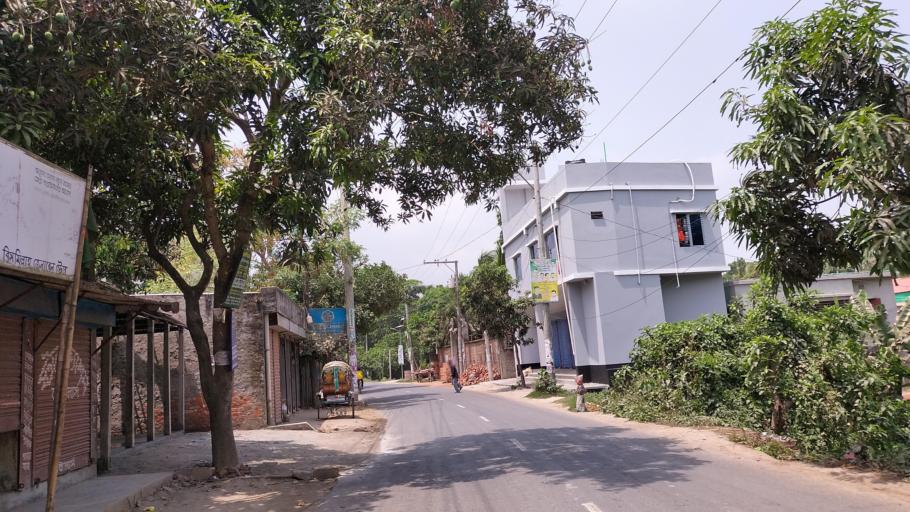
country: BD
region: Dhaka
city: Azimpur
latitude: 23.7293
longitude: 90.2891
